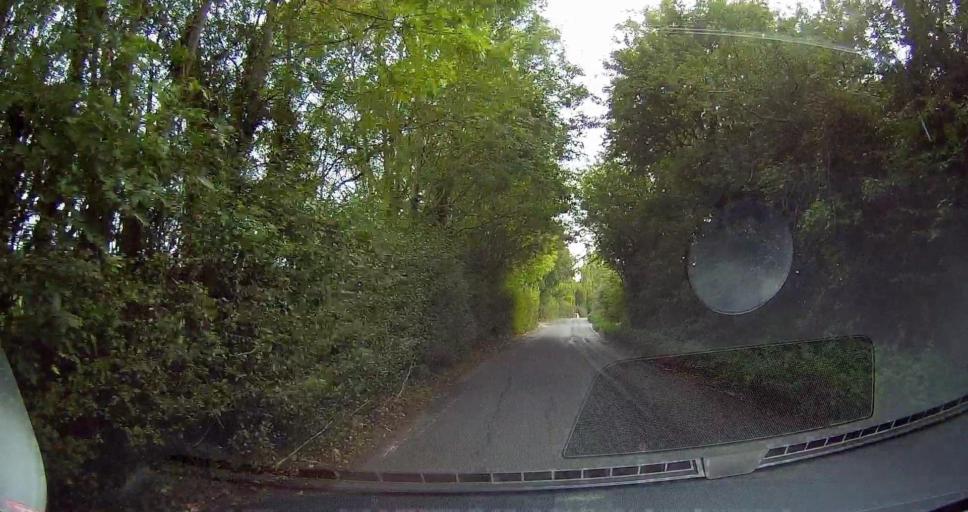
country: GB
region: England
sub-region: Kent
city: Hadlow
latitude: 51.2183
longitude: 0.3061
